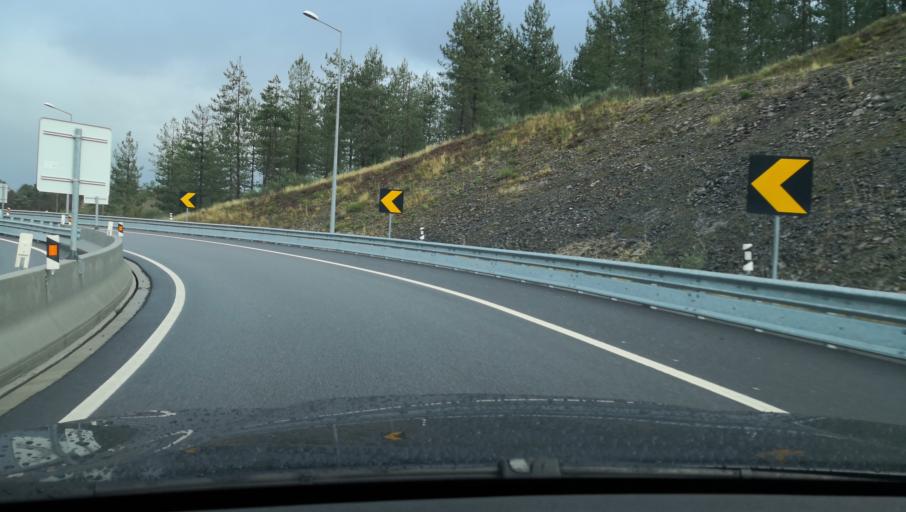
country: PT
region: Vila Real
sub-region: Santa Marta de Penaguiao
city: Santa Marta de Penaguiao
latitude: 41.2776
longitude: -7.8344
